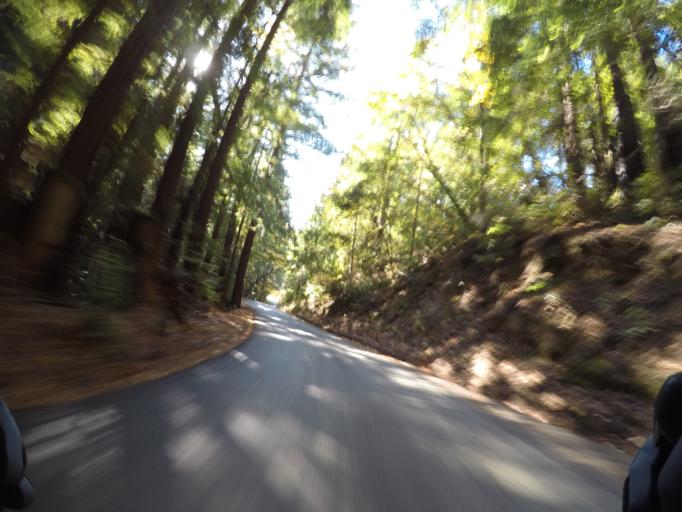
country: US
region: California
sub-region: Santa Clara County
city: Lexington Hills
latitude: 37.1480
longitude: -122.0187
